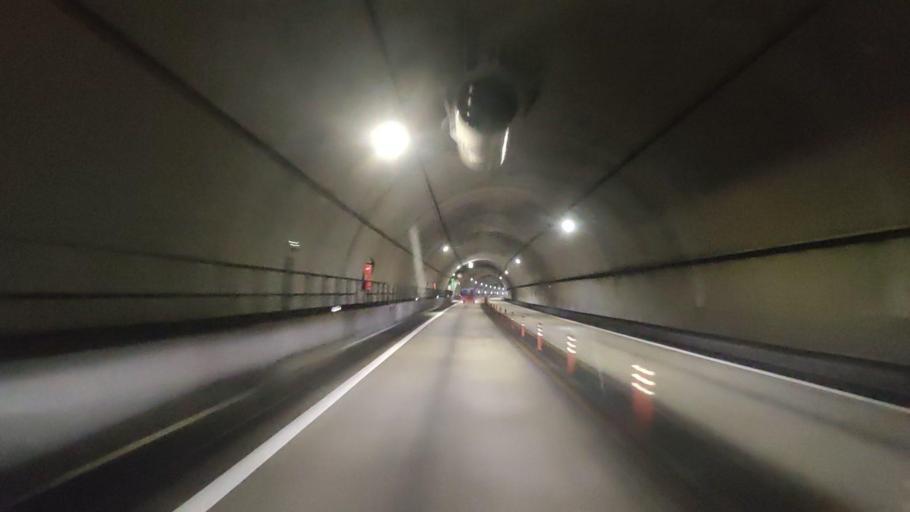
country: JP
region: Wakayama
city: Tanabe
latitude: 33.5490
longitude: 135.5169
